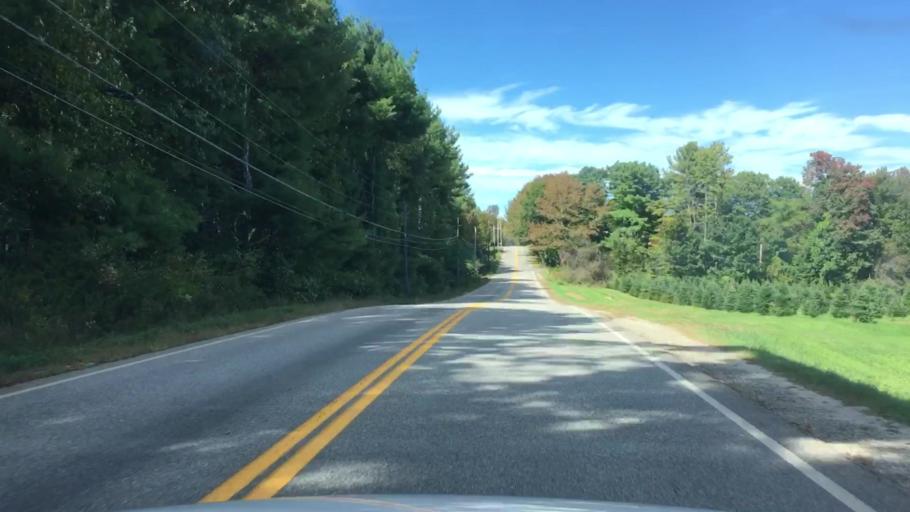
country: US
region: Maine
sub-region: Cumberland County
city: West Scarborough
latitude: 43.6167
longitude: -70.4060
